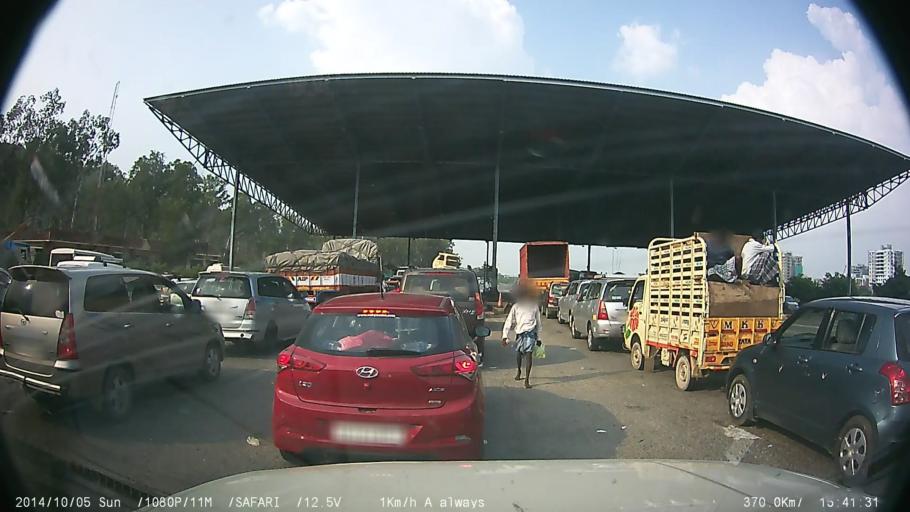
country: IN
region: Tamil Nadu
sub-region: Kancheepuram
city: Chengalpattu
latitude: 12.7234
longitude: 79.9817
